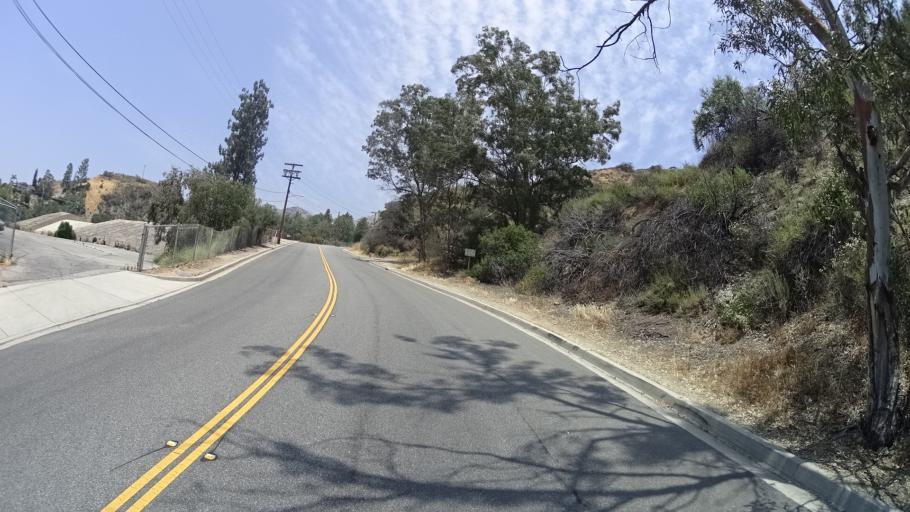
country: US
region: California
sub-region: Los Angeles County
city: Burbank
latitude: 34.1993
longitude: -118.3025
